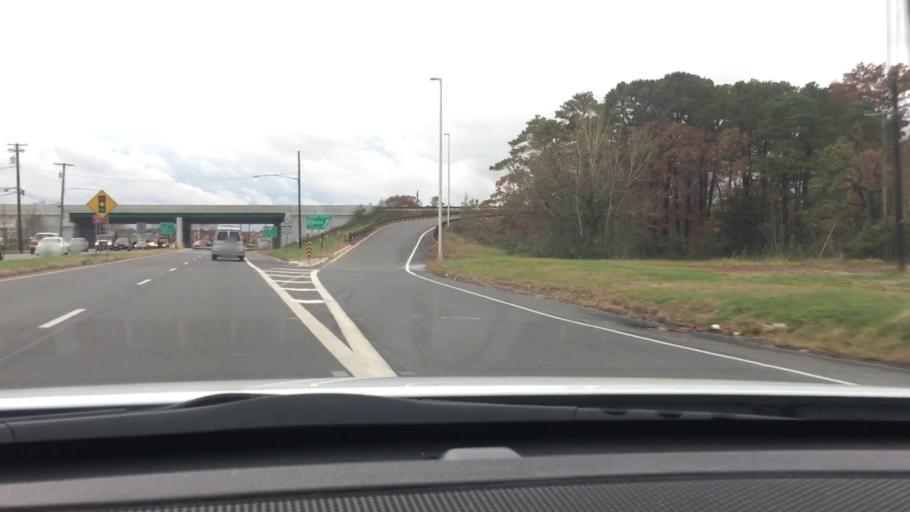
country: US
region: New Jersey
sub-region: Atlantic County
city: Northfield
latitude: 39.3997
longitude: -74.5578
